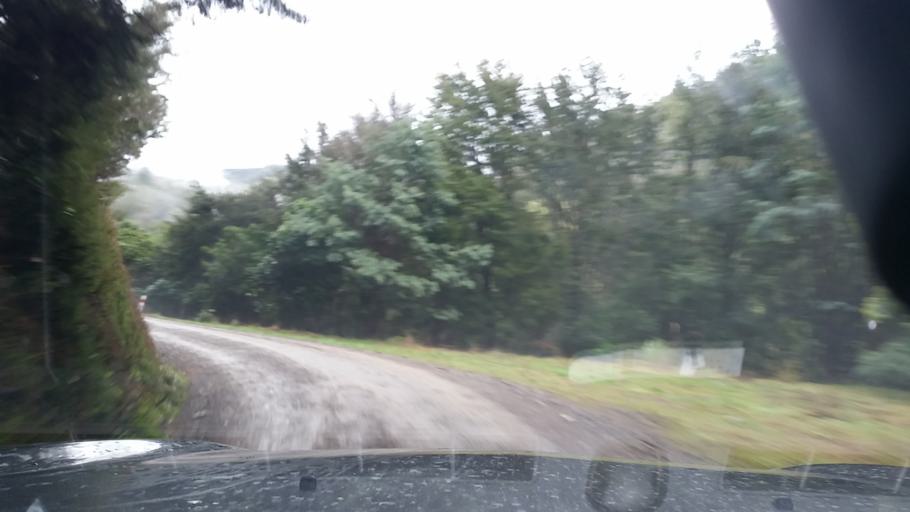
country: NZ
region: Nelson
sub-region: Nelson City
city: Nelson
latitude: -41.3730
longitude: 173.6013
